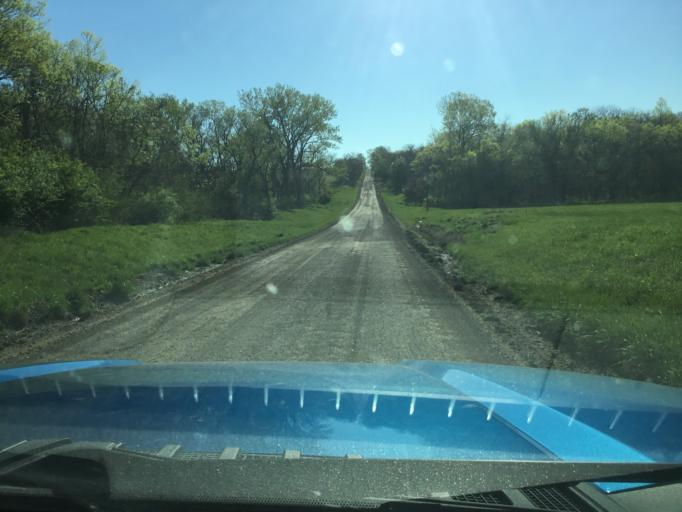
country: US
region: Kansas
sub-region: Douglas County
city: Lawrence
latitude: 38.9569
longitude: -95.3644
